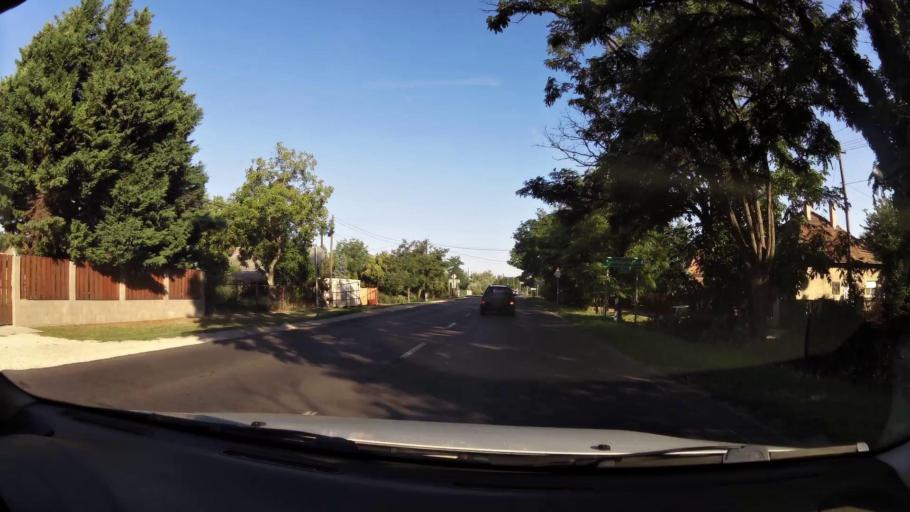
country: HU
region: Pest
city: Nyaregyhaza
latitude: 47.3066
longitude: 19.5041
